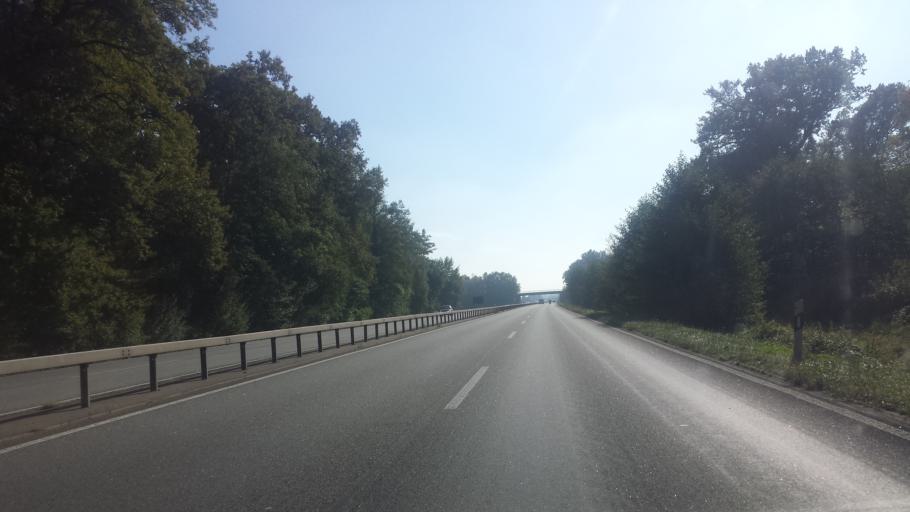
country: DE
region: Rheinland-Pfalz
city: Steinweiler
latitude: 49.1271
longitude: 8.1717
